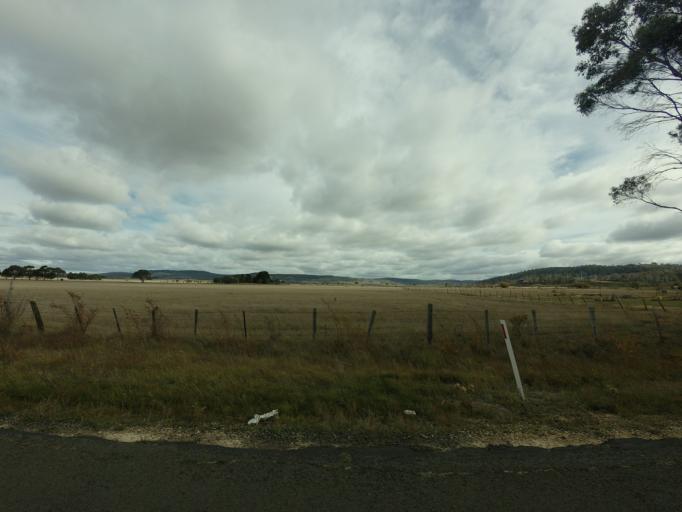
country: AU
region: Tasmania
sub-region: Brighton
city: Bridgewater
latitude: -42.4042
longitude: 147.3928
